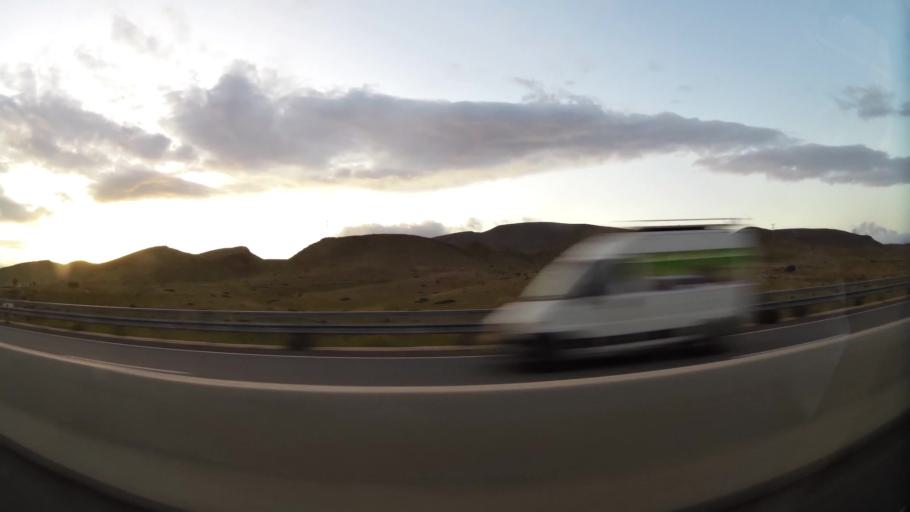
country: MA
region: Oriental
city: El Aioun
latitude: 34.5986
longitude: -2.6407
